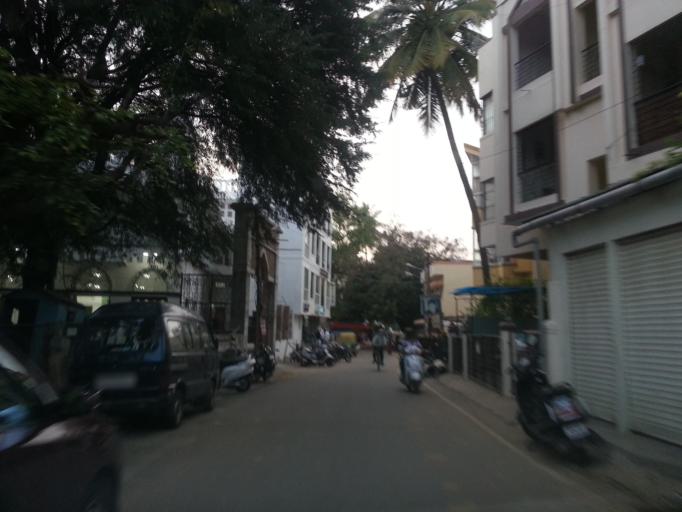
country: IN
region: Karnataka
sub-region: Bangalore Urban
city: Bangalore
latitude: 13.0033
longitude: 77.6233
